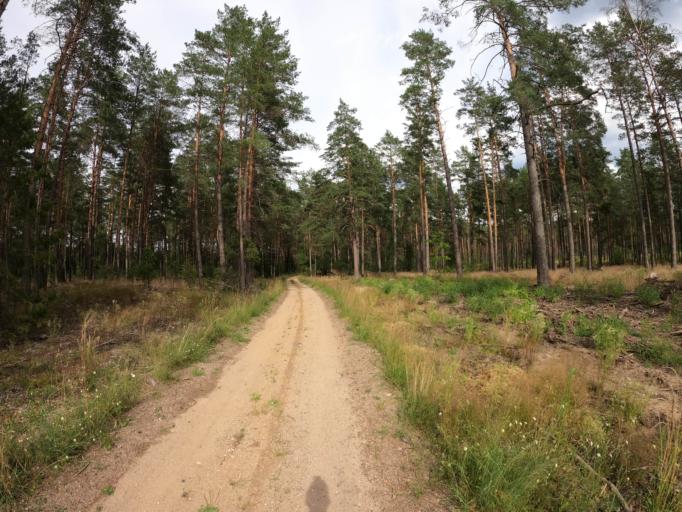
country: LT
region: Alytaus apskritis
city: Druskininkai
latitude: 54.0658
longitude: 24.0933
